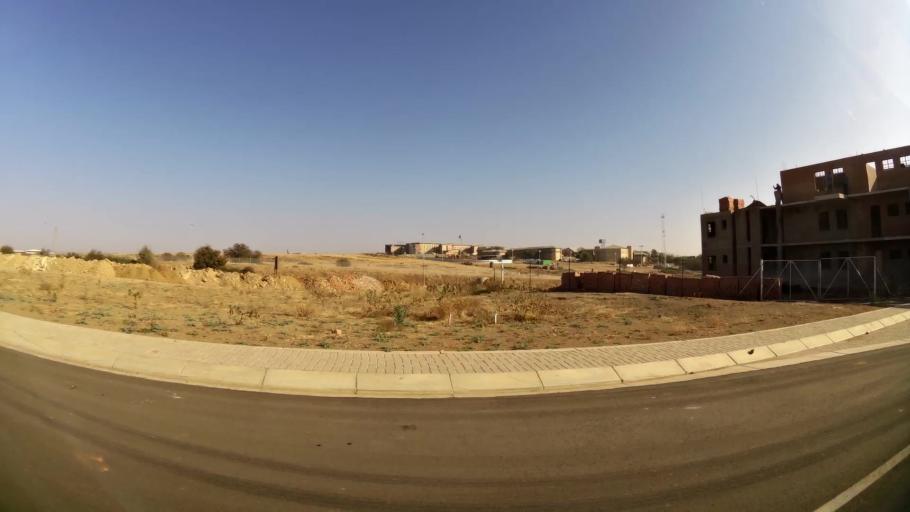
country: ZA
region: Orange Free State
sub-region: Mangaung Metropolitan Municipality
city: Bloemfontein
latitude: -29.1863
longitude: 26.2171
